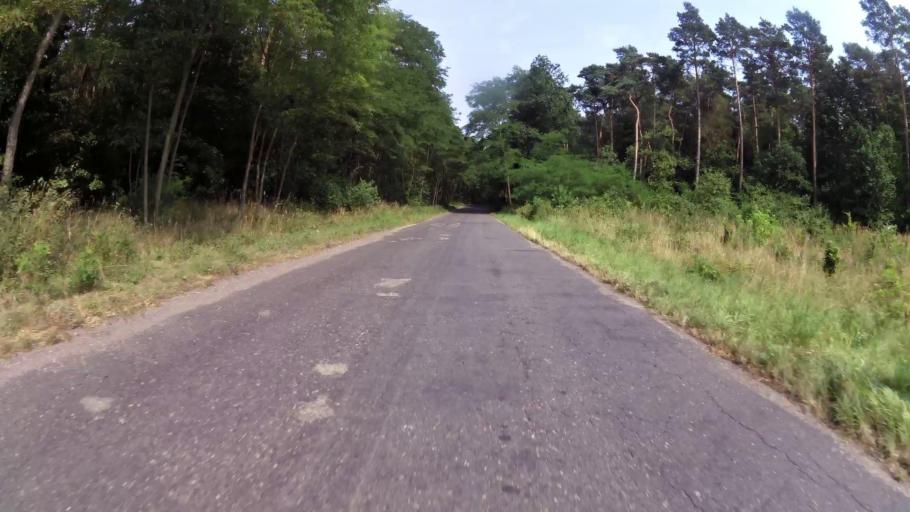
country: PL
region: West Pomeranian Voivodeship
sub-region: Powiat mysliborski
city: Debno
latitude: 52.8515
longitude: 14.6907
